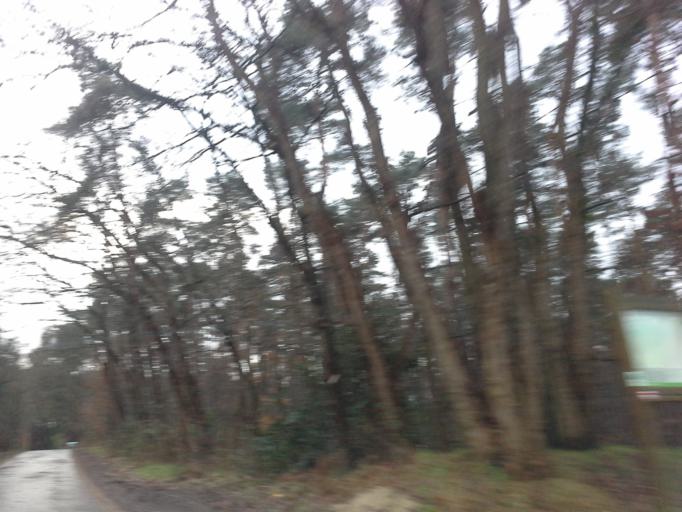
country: BE
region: Flanders
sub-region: Provincie Antwerpen
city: Meerhout
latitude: 51.1425
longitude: 5.0540
